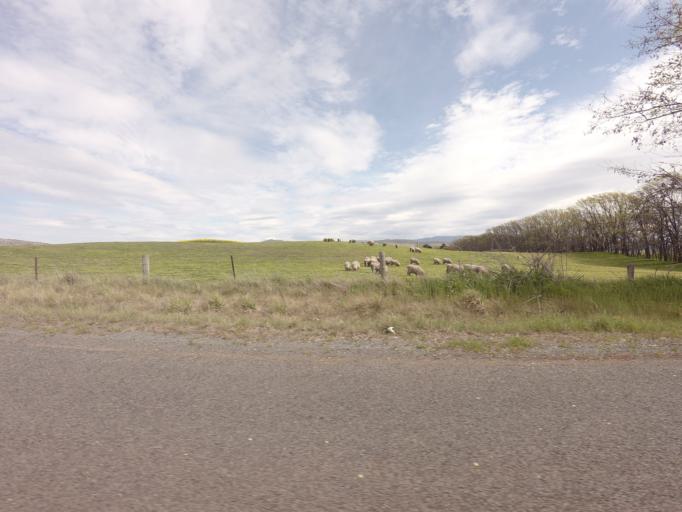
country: AU
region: Tasmania
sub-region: Northern Midlands
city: Evandale
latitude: -41.8793
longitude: 147.3605
